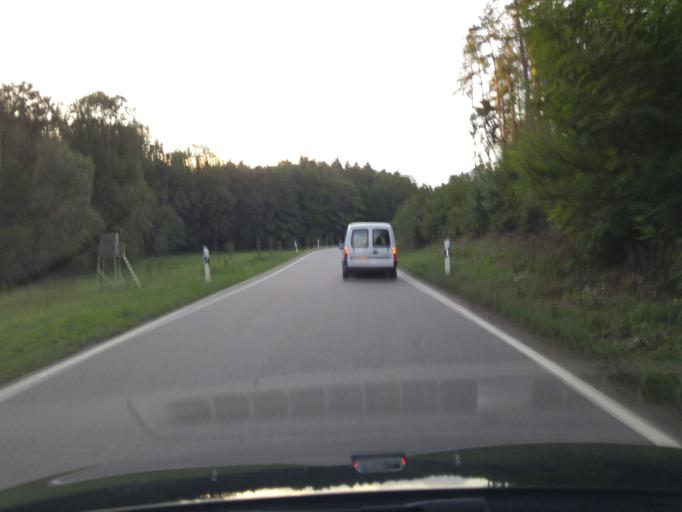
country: DE
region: Baden-Wuerttemberg
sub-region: Regierungsbezirk Stuttgart
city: Bad Rappenau
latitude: 49.2076
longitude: 9.1194
